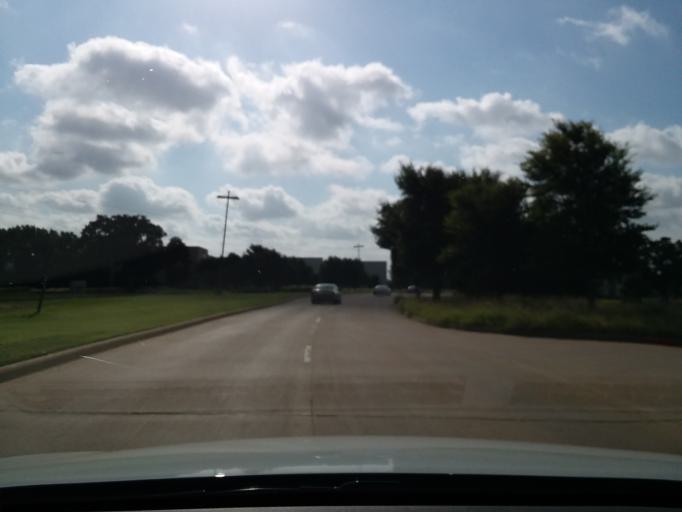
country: US
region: Texas
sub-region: Dallas County
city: Coppell
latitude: 32.9947
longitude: -97.0410
